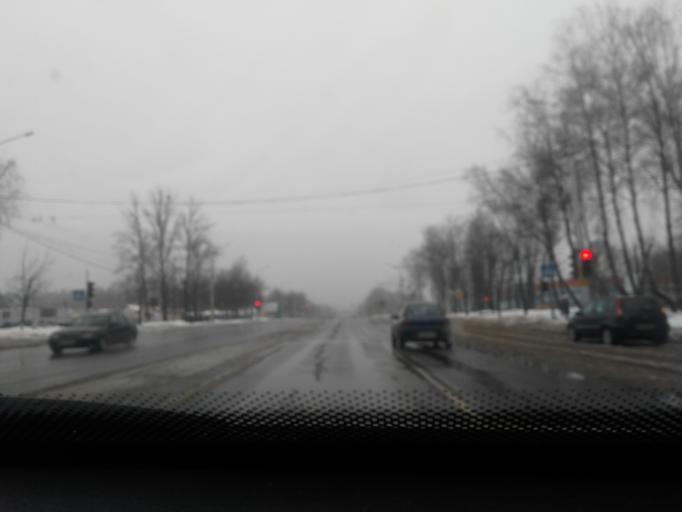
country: BY
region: Mogilev
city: Babruysk
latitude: 53.1721
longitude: 29.2032
